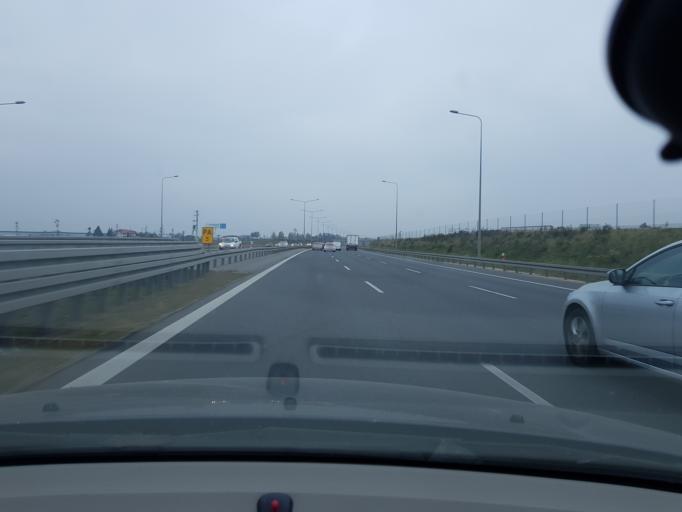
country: PL
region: Masovian Voivodeship
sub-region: Powiat pruszkowski
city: Michalowice
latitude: 52.1370
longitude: 20.8811
